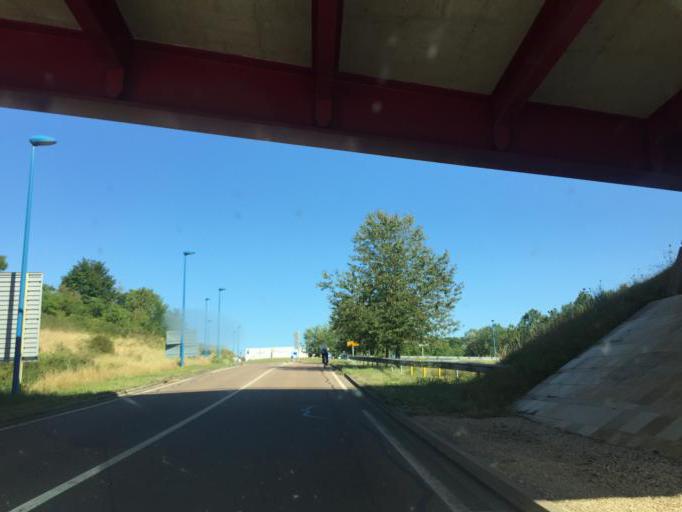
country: FR
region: Bourgogne
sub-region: Departement de la Nievre
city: Clamecy
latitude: 47.4484
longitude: 3.4879
